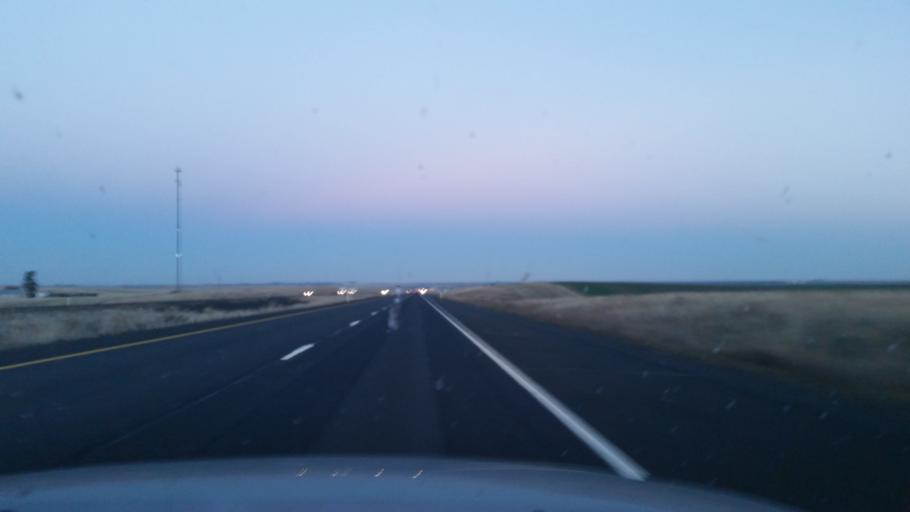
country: US
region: Washington
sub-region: Adams County
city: Ritzville
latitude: 47.1111
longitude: -118.4605
